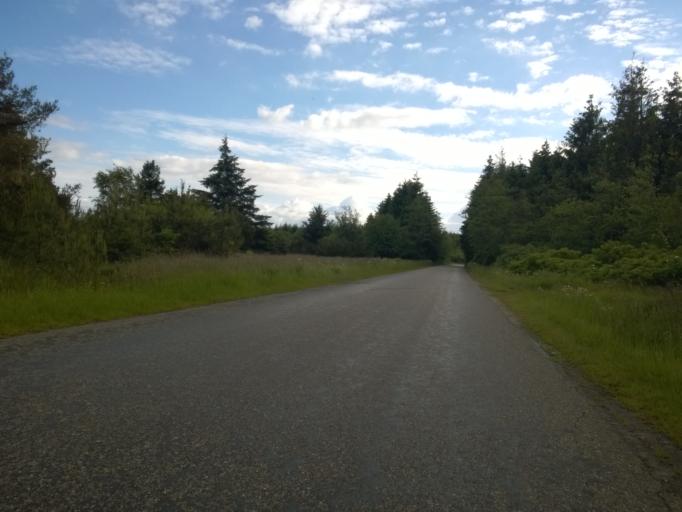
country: DK
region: Central Jutland
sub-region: Holstebro Kommune
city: Vinderup
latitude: 56.5126
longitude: 8.8260
